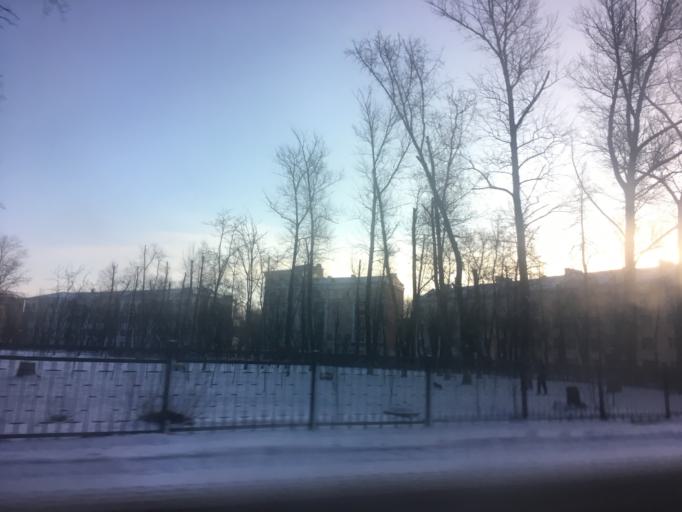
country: RU
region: Tula
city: Tula
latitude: 54.2108
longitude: 37.6628
